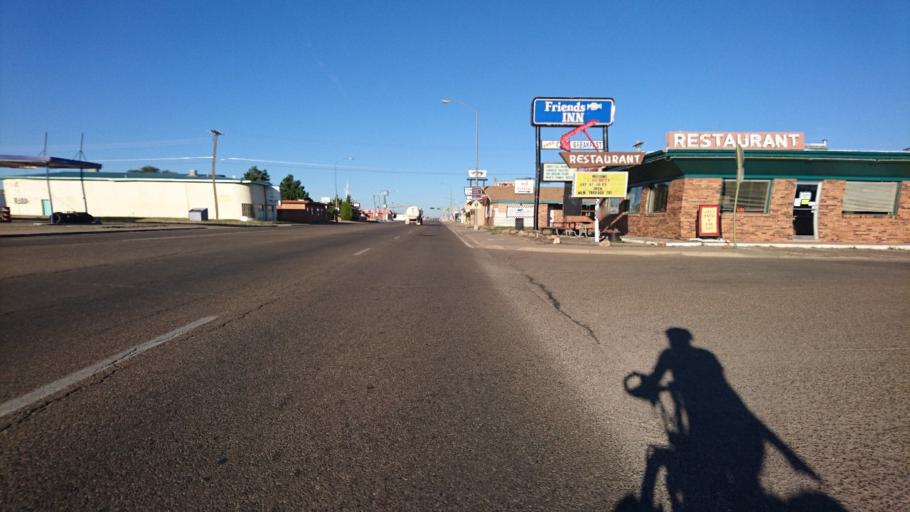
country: US
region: New Mexico
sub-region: Quay County
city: Tucumcari
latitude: 35.1719
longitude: -103.7222
